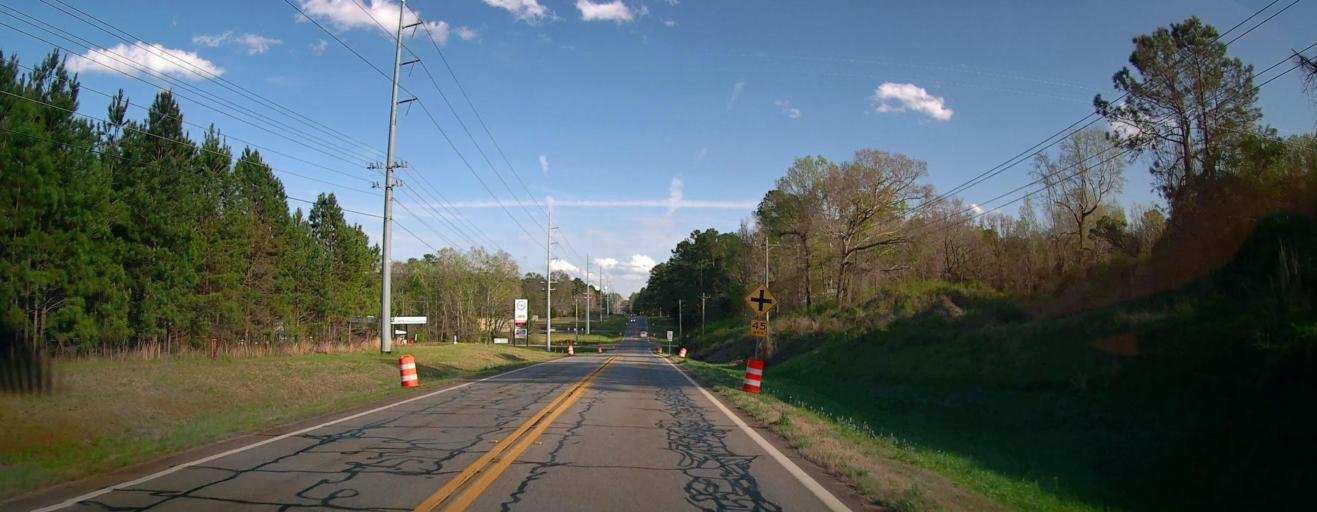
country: US
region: Georgia
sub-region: Baldwin County
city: Milledgeville
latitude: 33.1553
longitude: -83.3490
